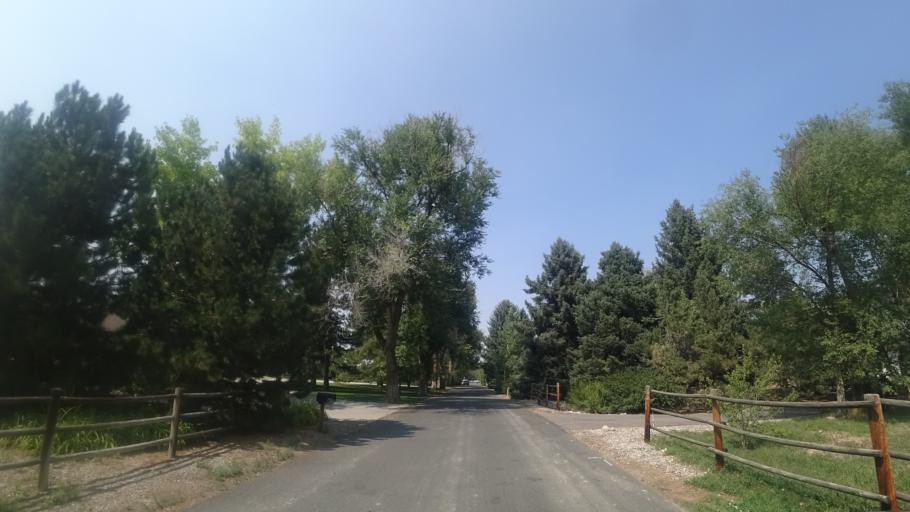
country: US
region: Colorado
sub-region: Arapahoe County
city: Cherry Hills Village
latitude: 39.6353
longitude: -104.9738
